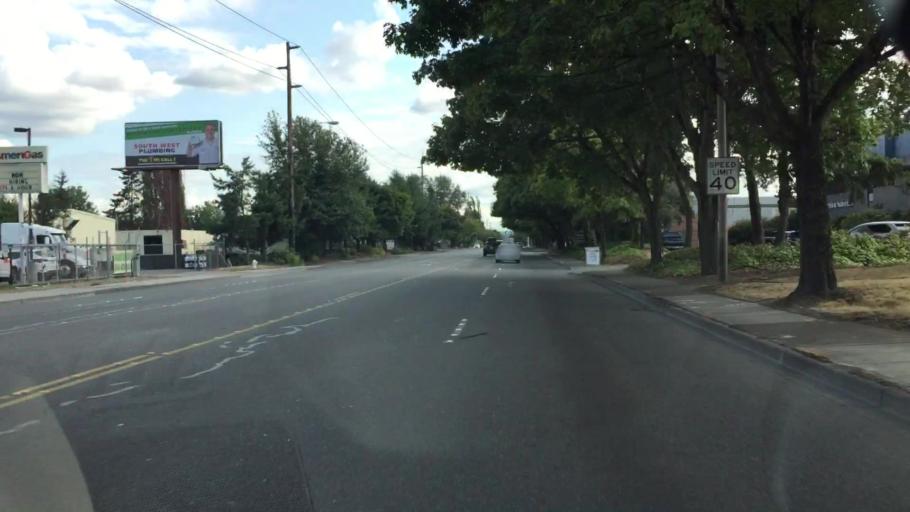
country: US
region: Washington
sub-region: King County
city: Kent
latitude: 47.4293
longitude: -122.2281
